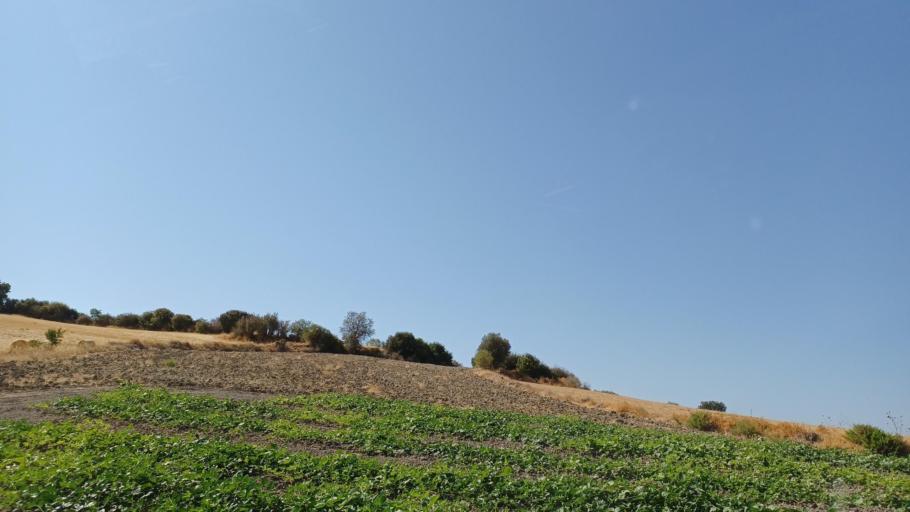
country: CY
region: Pafos
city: Polis
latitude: 34.9688
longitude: 32.4877
